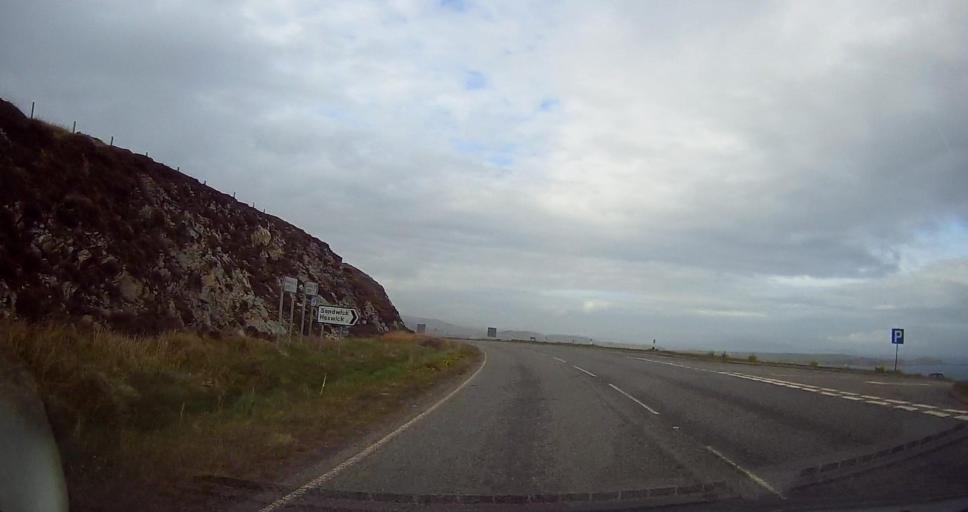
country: GB
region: Scotland
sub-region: Shetland Islands
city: Sandwick
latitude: 60.0173
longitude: -1.2315
